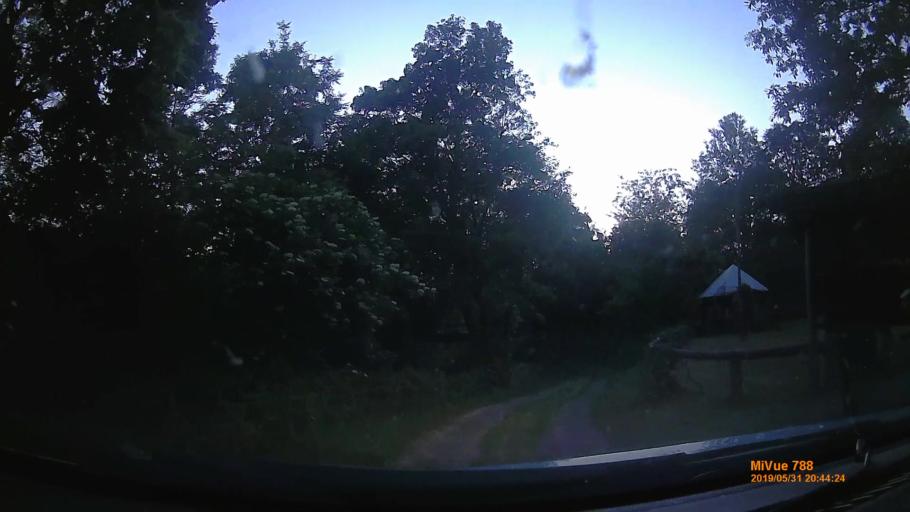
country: HU
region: Nograd
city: Nagyoroszi
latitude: 48.0262
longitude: 19.0493
